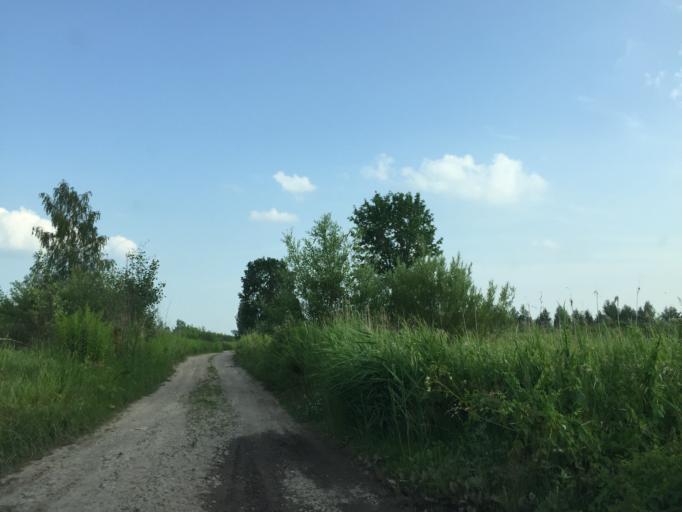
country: LV
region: Jelgava
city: Jelgava
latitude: 56.6717
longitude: 23.7112
